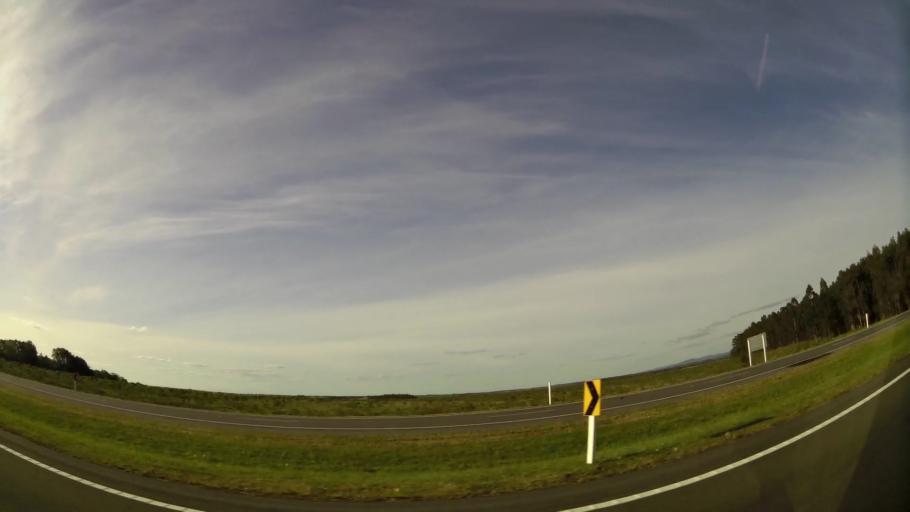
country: UY
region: Lavalleja
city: Solis de Mataojo
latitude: -34.7778
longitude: -55.4598
